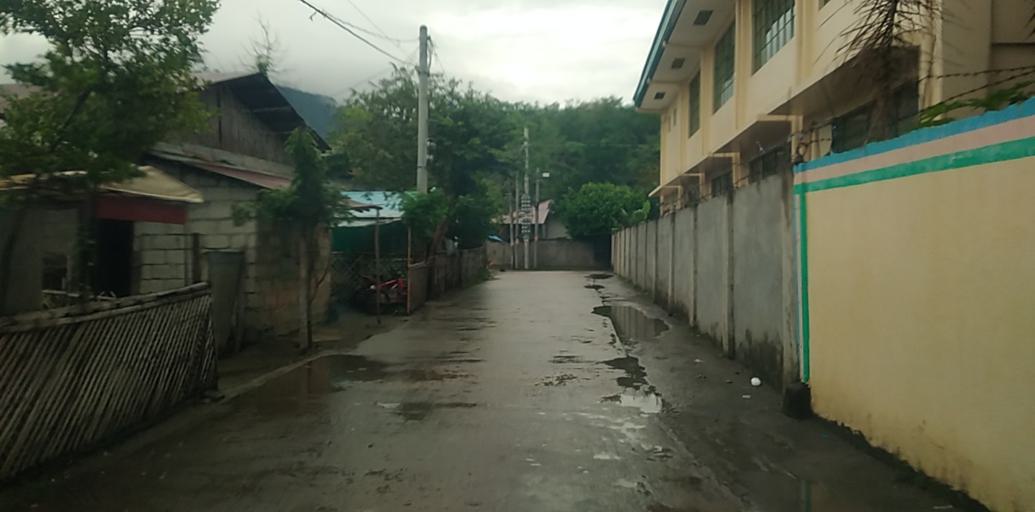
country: PH
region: Central Luzon
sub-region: Province of Pampanga
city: Arayat
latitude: 15.1527
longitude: 120.7406
